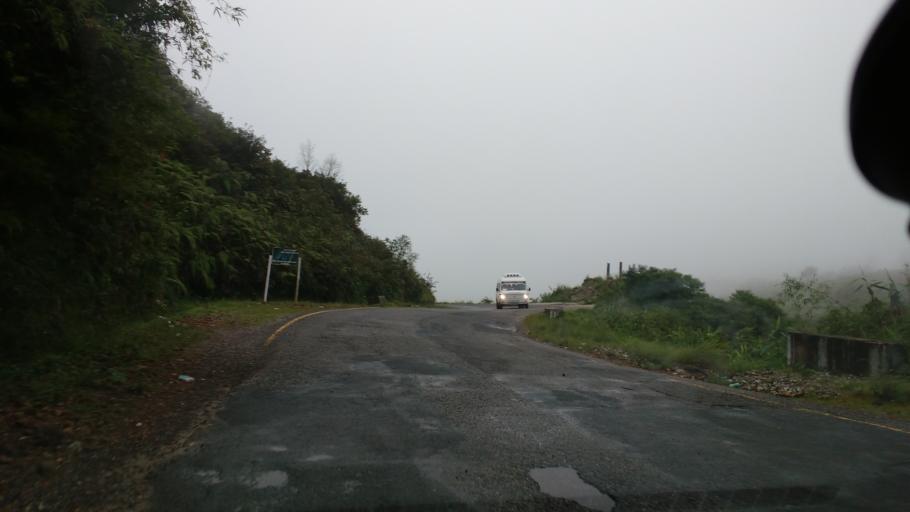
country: IN
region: Meghalaya
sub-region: East Khasi Hills
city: Cherrapunji
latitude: 25.2944
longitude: 91.7175
